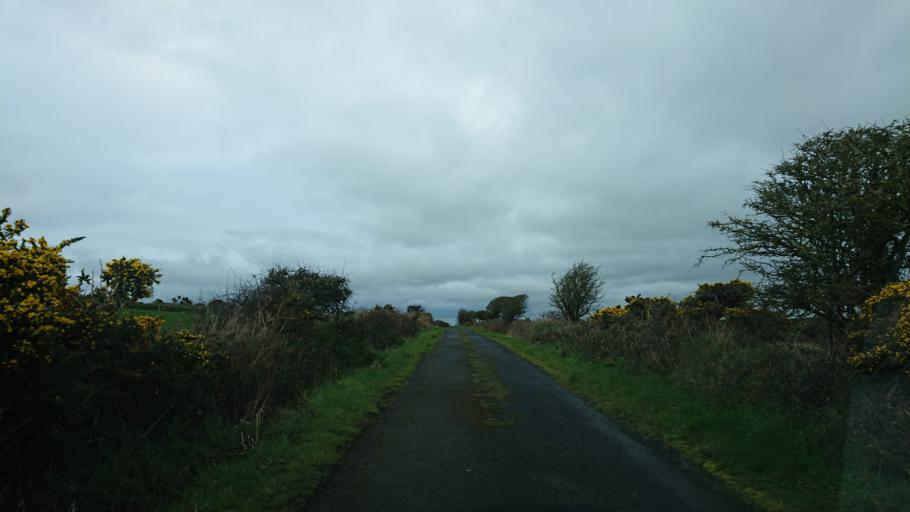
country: IE
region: Munster
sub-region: Waterford
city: Dunmore East
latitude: 52.1466
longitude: -7.0405
